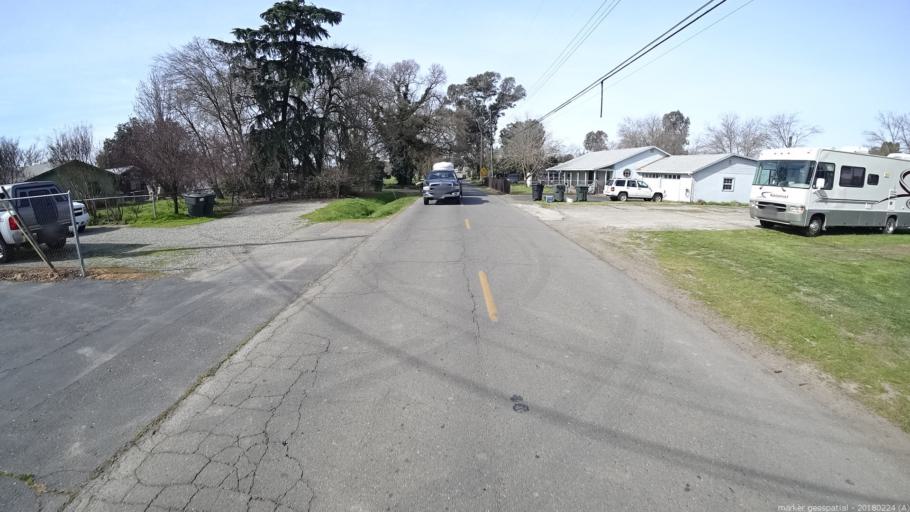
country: US
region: California
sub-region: Sacramento County
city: Rio Linda
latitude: 38.6728
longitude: -121.4356
